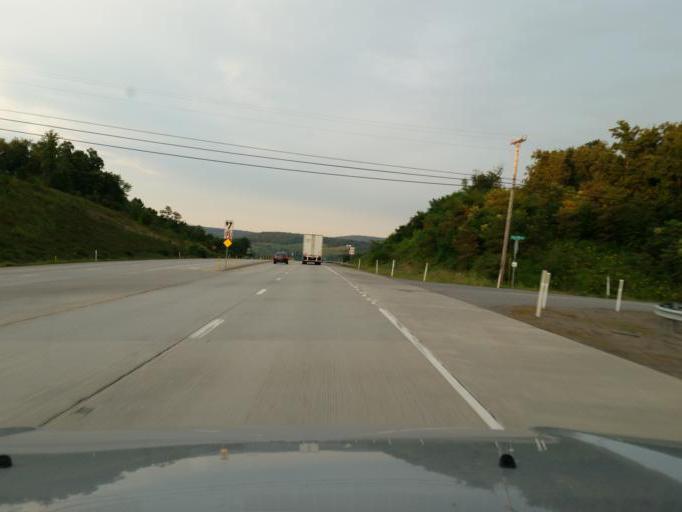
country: US
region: Pennsylvania
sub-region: Indiana County
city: Homer City
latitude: 40.4477
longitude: -79.0689
